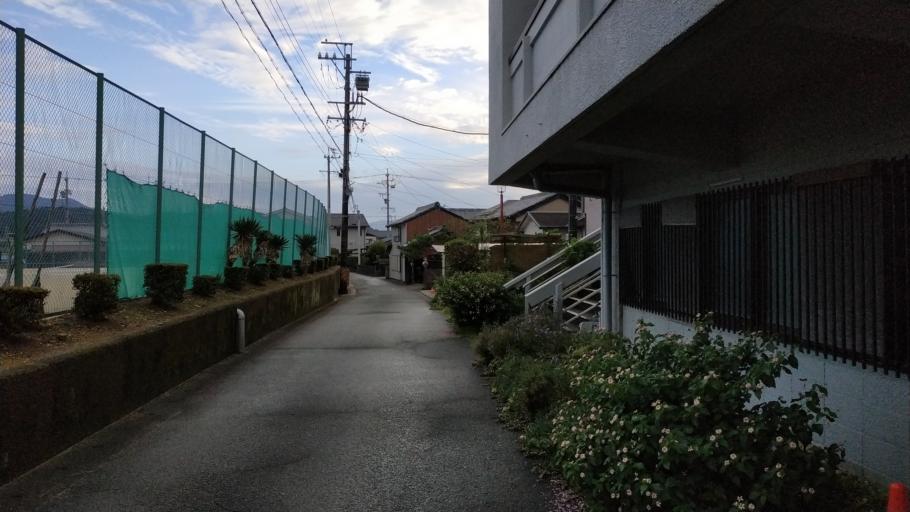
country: JP
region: Mie
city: Toba
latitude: 34.5100
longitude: 136.7713
